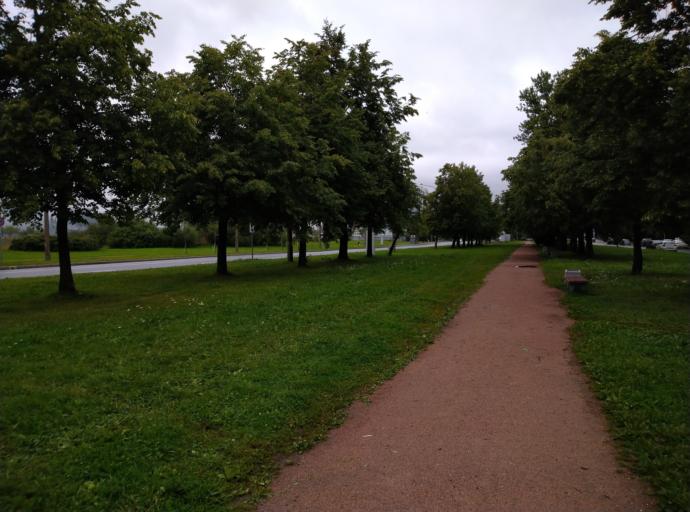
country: RU
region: St.-Petersburg
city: Kupchino
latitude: 59.8464
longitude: 30.3556
